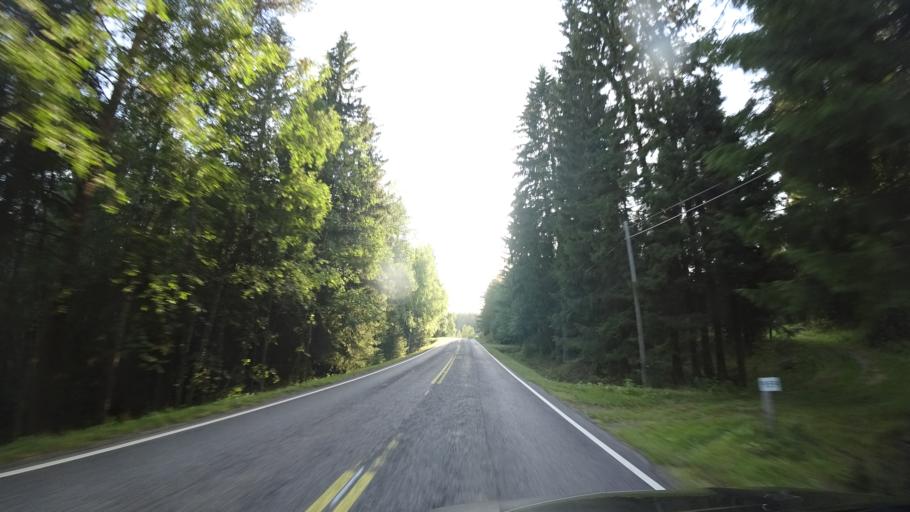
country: FI
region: Haeme
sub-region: Haemeenlinna
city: Lammi
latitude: 61.0066
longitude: 24.8748
